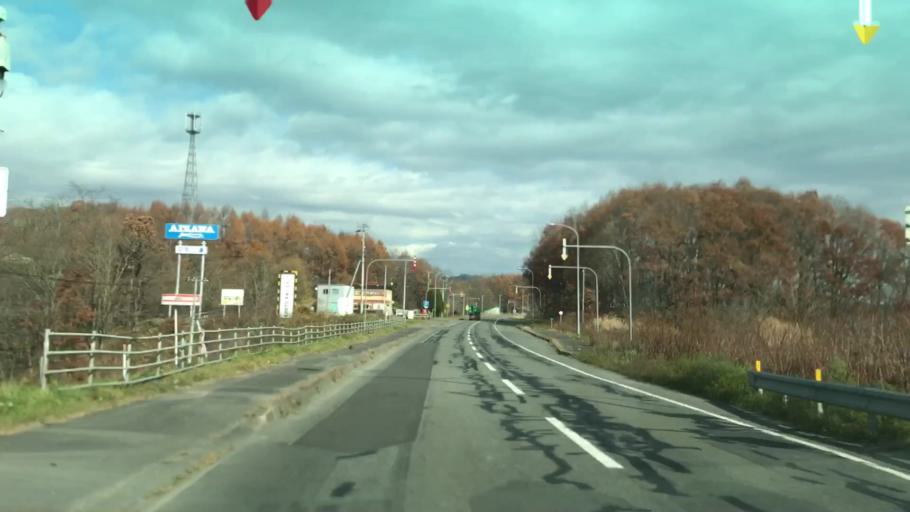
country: JP
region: Hokkaido
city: Shizunai-furukawacho
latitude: 42.6927
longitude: 142.2157
